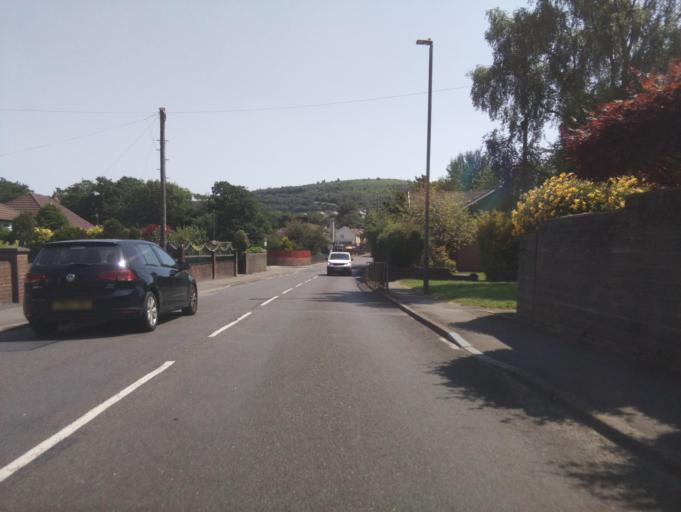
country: GB
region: Wales
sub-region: Caerphilly County Borough
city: Caerphilly
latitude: 51.5729
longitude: -3.2330
